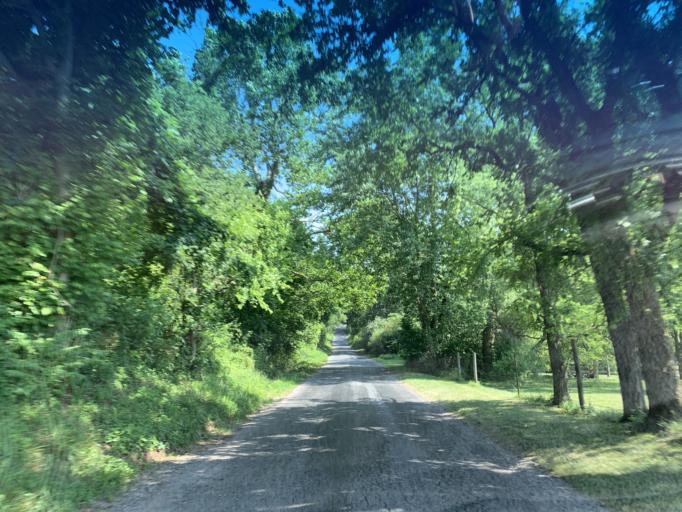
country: US
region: Maryland
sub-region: Montgomery County
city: Poolesville
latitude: 39.1373
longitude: -77.4501
